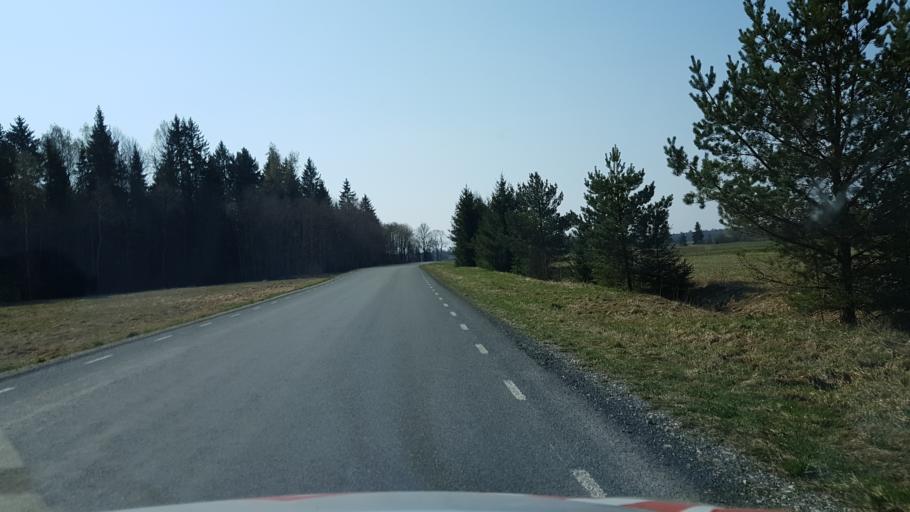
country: EE
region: Raplamaa
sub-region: Maerjamaa vald
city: Marjamaa
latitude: 58.8646
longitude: 24.3718
